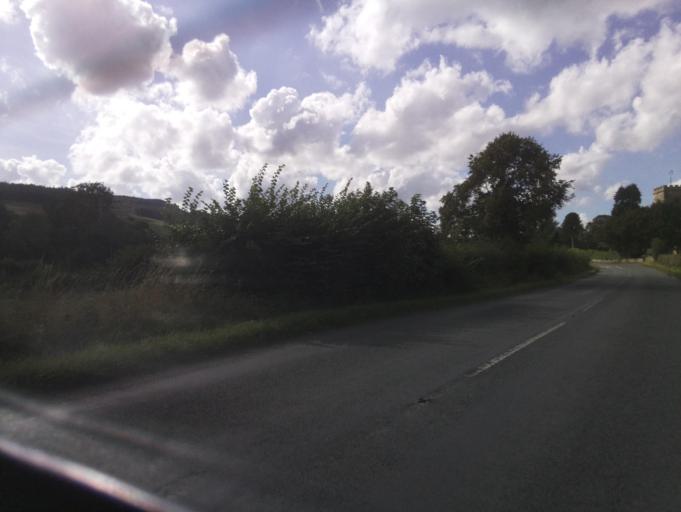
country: GB
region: England
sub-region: North Yorkshire
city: Leyburn
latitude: 54.2691
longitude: -1.7740
